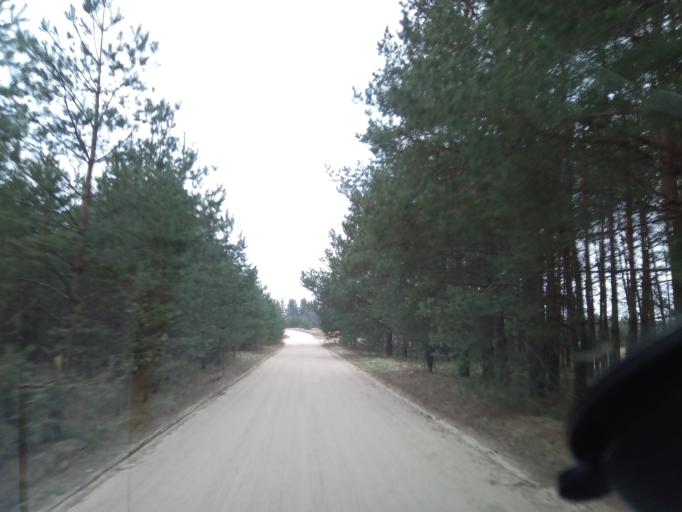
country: LT
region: Alytaus apskritis
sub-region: Alytaus rajonas
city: Daugai
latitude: 54.3611
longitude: 24.4416
